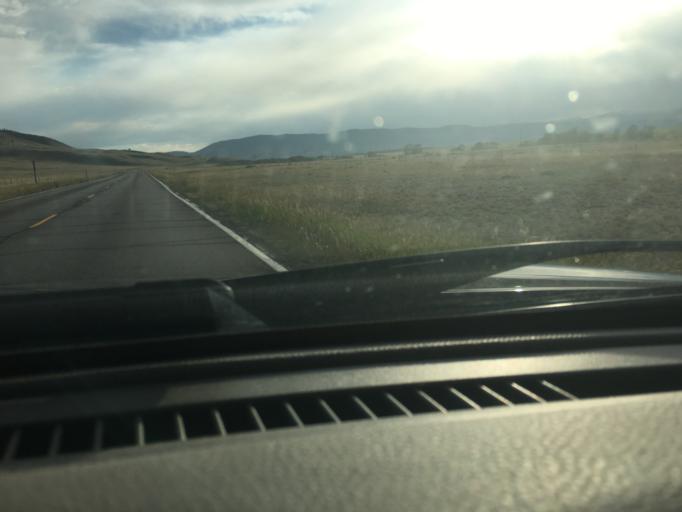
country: US
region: Wyoming
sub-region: Albany County
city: Laramie
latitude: 41.2903
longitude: -106.0313
